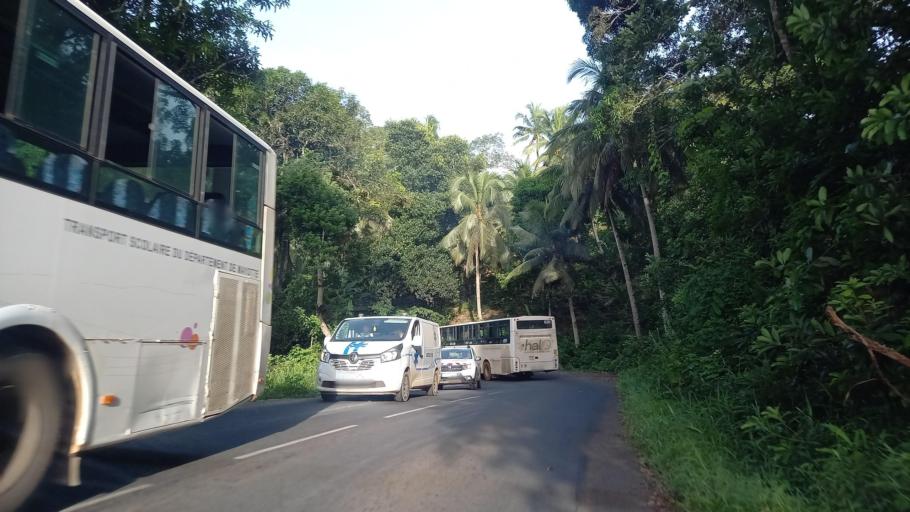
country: YT
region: Bandraboua
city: Bandraboua
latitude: -12.7372
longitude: 45.1182
